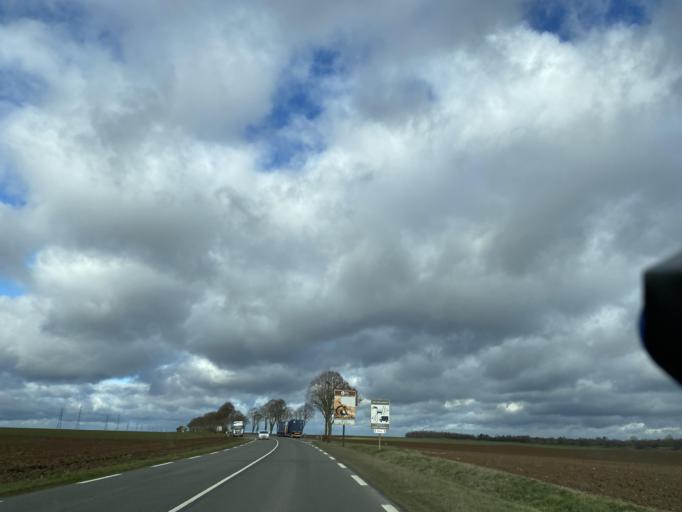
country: FR
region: Centre
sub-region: Departement d'Eure-et-Loir
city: Baigneaux
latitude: 48.1356
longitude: 1.8512
